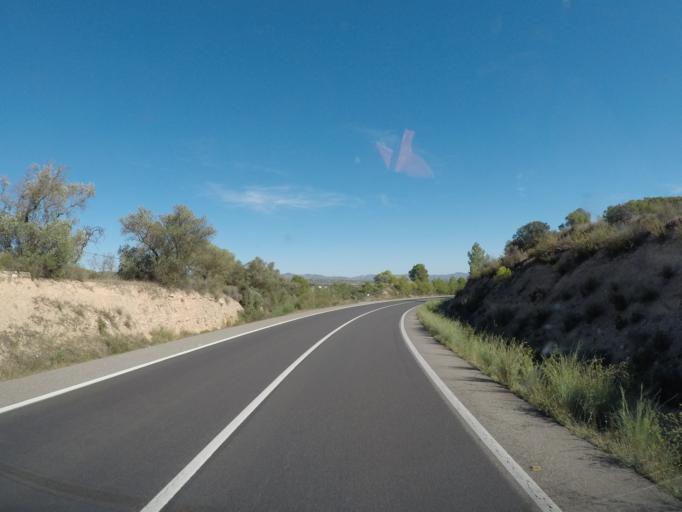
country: ES
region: Catalonia
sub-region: Provincia de Tarragona
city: Miravet
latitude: 41.0294
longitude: 0.6041
